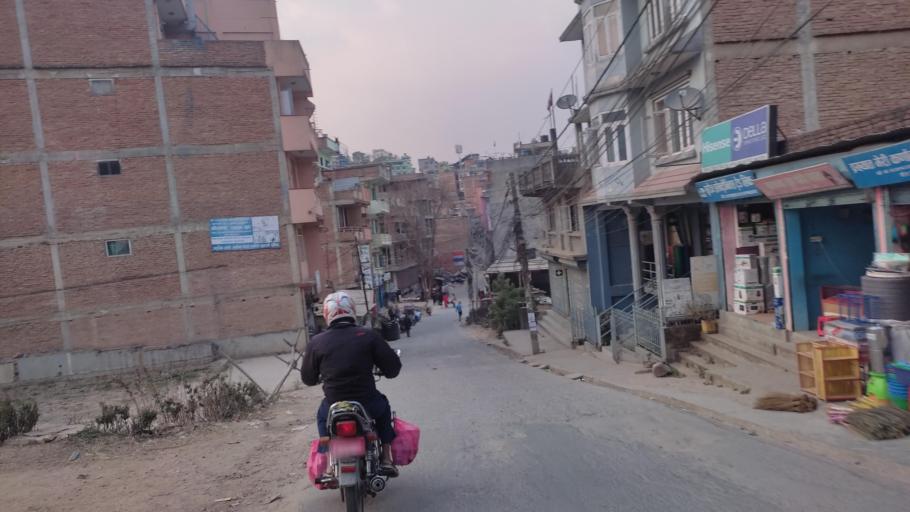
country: NP
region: Central Region
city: Kirtipur
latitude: 27.6723
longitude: 85.2796
